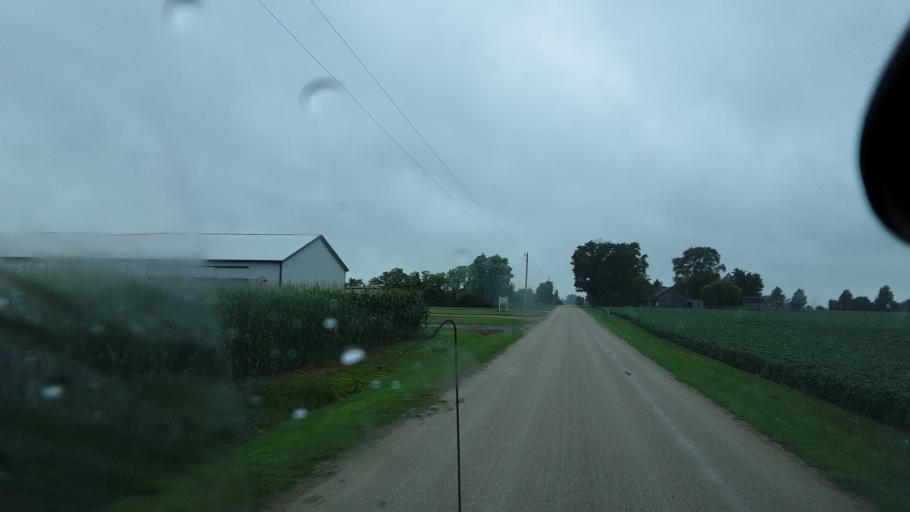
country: US
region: Indiana
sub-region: Adams County
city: Berne
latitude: 40.7029
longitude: -84.8433
